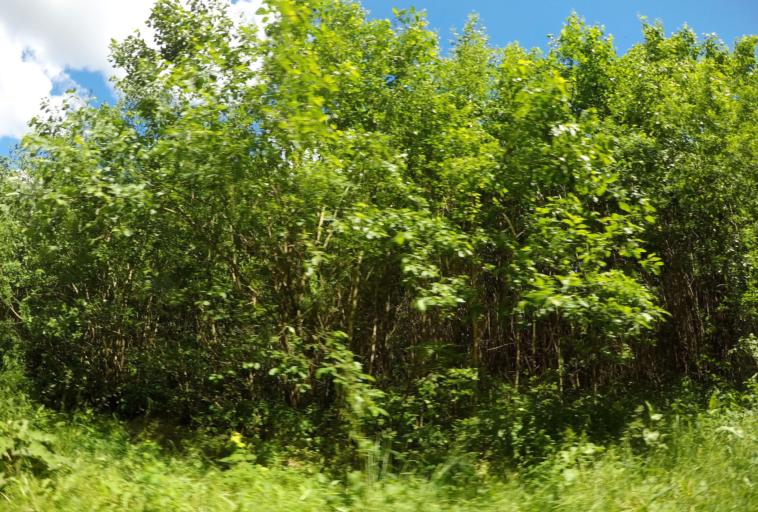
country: BY
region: Grodnenskaya
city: Hal'shany
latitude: 54.2338
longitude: 26.0329
